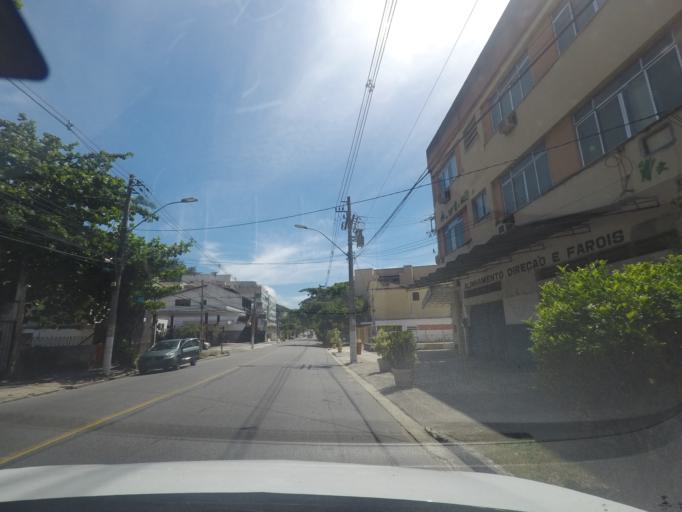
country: BR
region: Rio de Janeiro
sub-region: Niteroi
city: Niteroi
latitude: -22.9165
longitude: -43.0848
